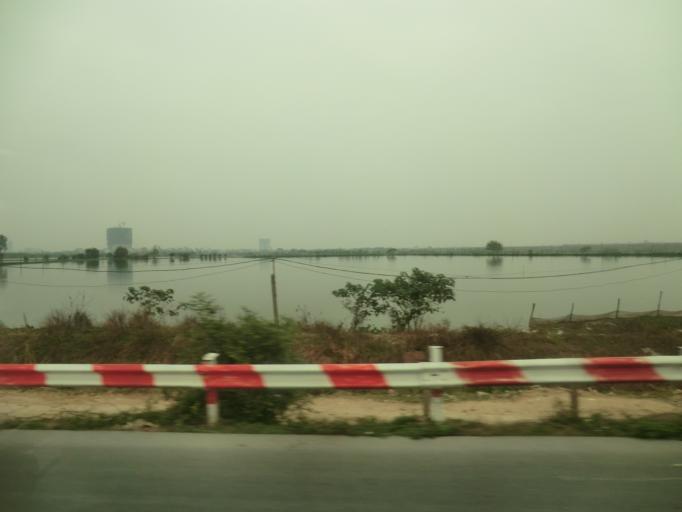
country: VN
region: Ha Noi
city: Van Dien
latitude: 20.9474
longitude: 105.8568
